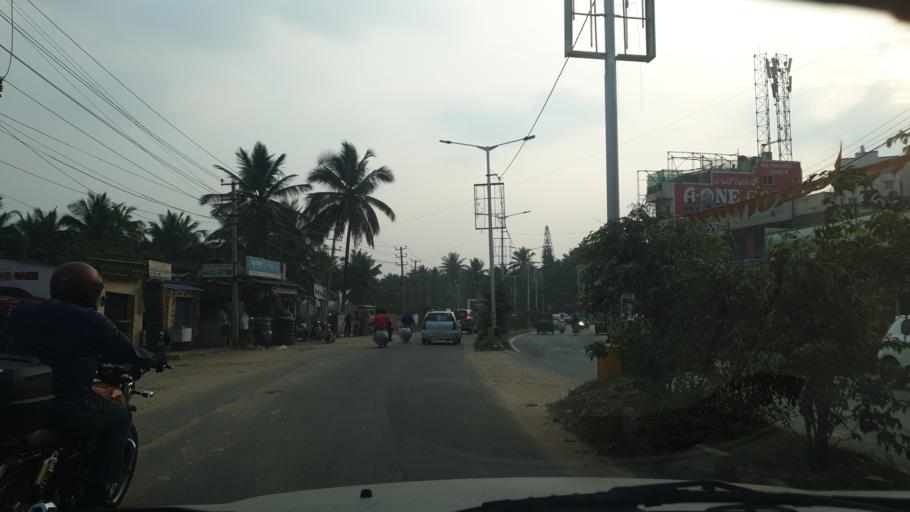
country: IN
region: Karnataka
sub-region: Bangalore Urban
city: Yelahanka
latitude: 13.0483
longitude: 77.6453
